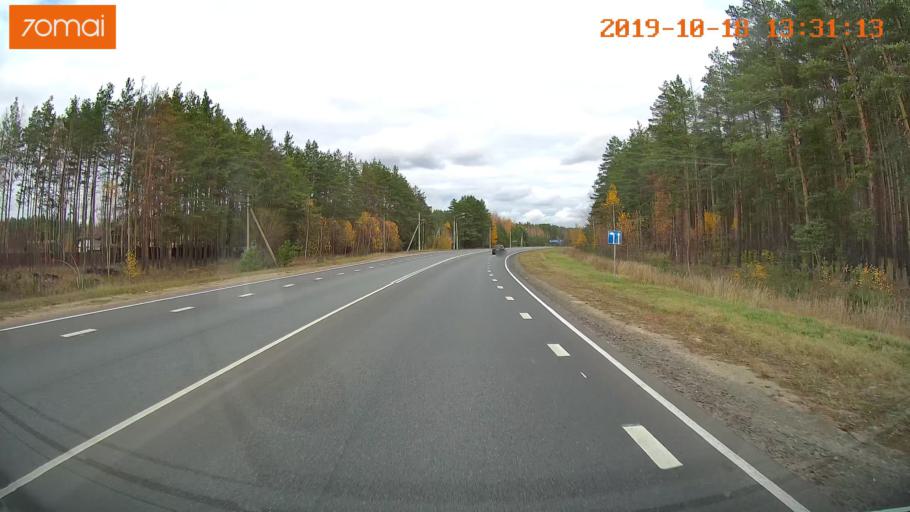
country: RU
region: Rjazan
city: Solotcha
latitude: 54.8198
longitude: 39.8966
